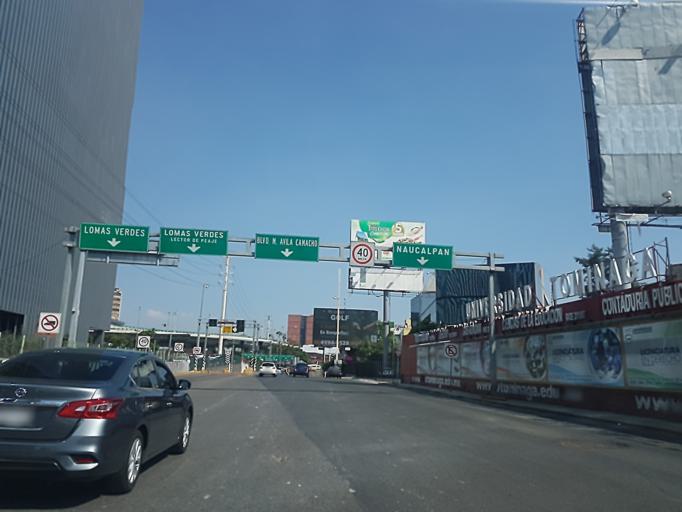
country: MX
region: Mexico City
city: Miguel Hidalgo
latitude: 19.4552
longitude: -99.2184
